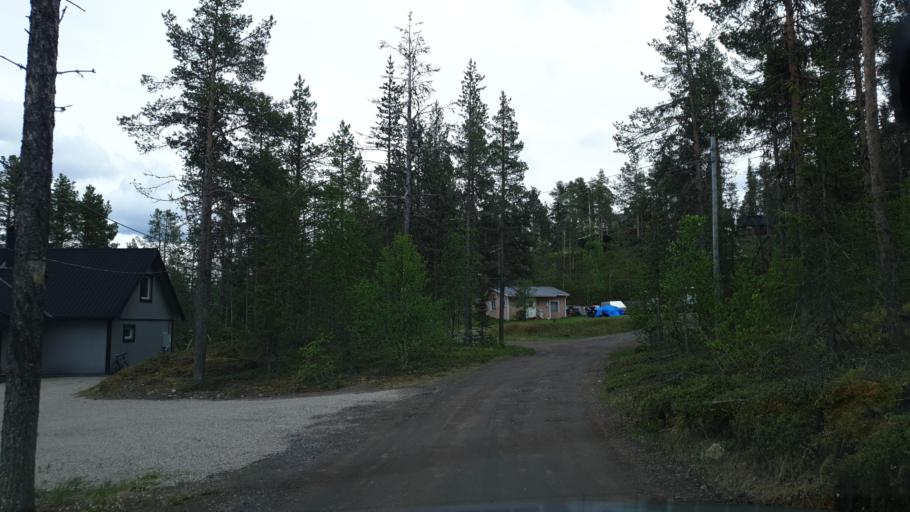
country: SE
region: Norrbotten
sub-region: Kiruna Kommun
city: Kiruna
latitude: 67.8498
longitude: 20.5330
